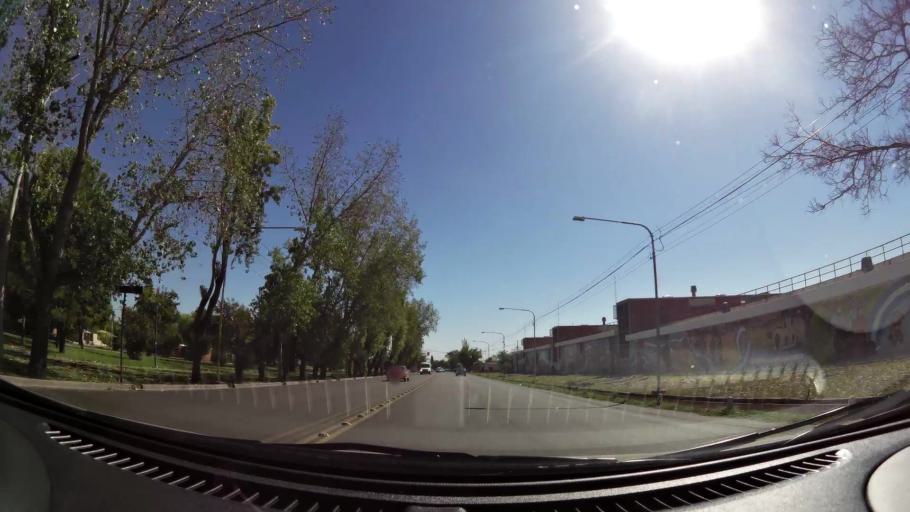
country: AR
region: Mendoza
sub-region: Departamento de Maipu
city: Maipu
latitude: -32.9712
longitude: -68.7931
